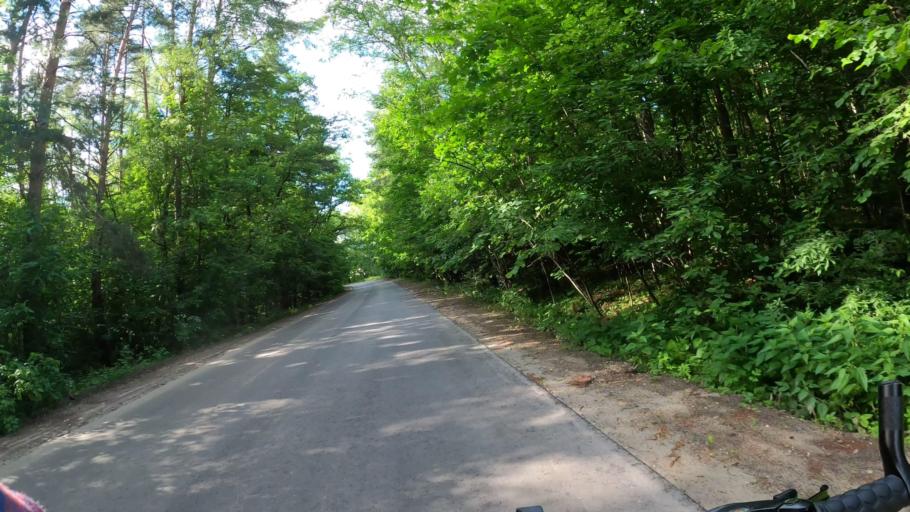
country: RU
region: Moskovskaya
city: Ashitkovo
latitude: 55.4378
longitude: 38.6330
